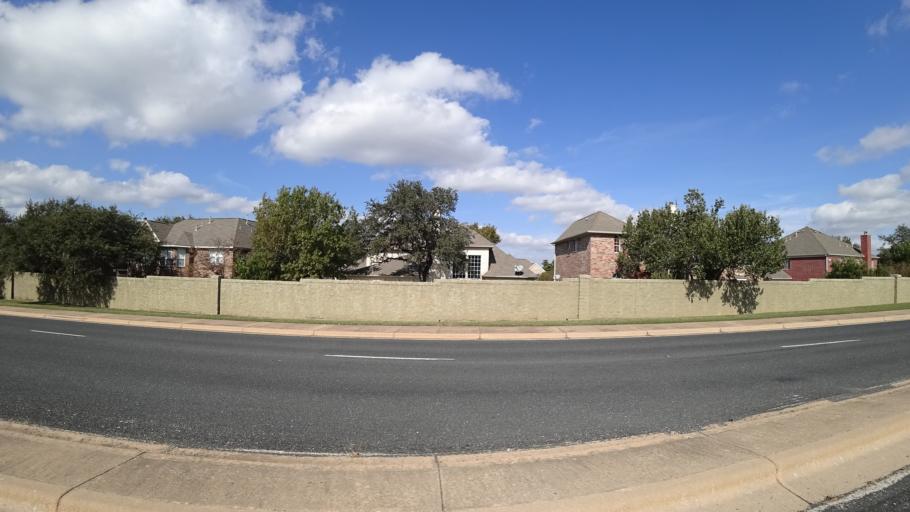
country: US
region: Texas
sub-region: Williamson County
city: Jollyville
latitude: 30.4225
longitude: -97.7868
